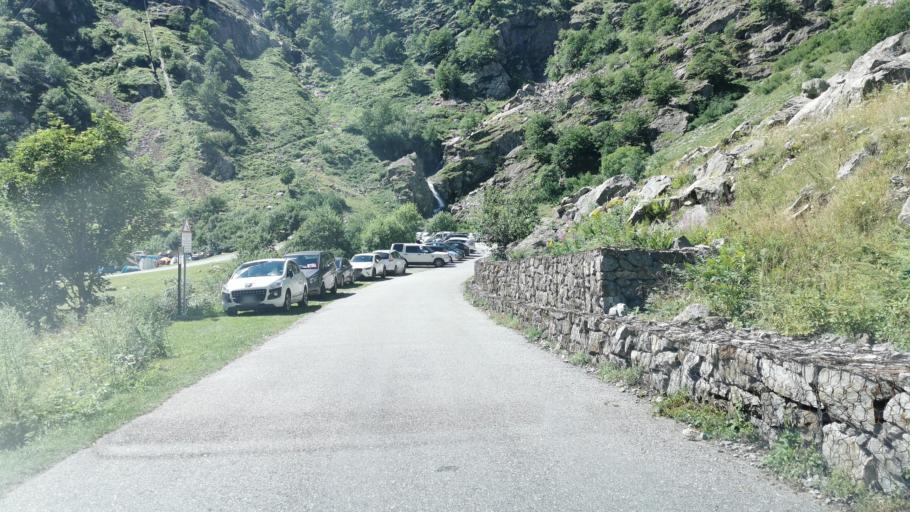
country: IT
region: Piedmont
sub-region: Provincia di Cuneo
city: Entracque
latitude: 44.1749
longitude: 7.3405
